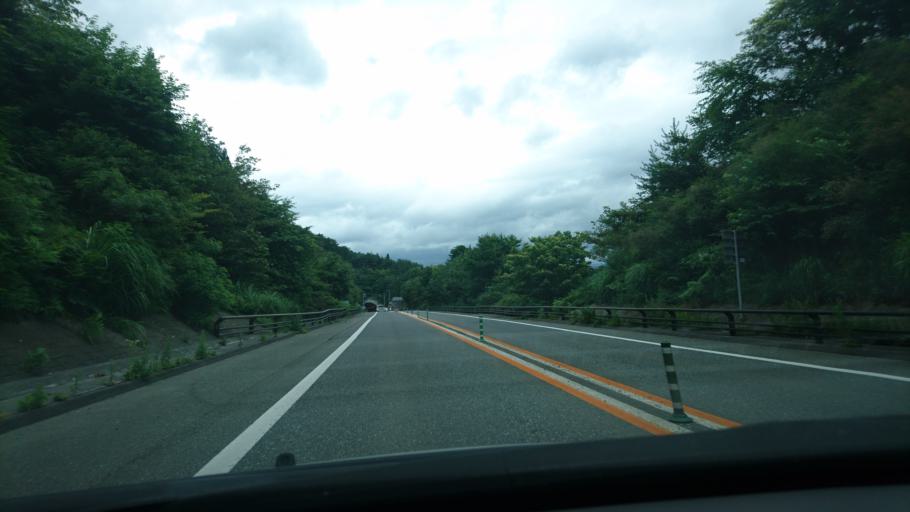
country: JP
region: Iwate
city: Ofunato
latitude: 39.0516
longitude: 141.7142
